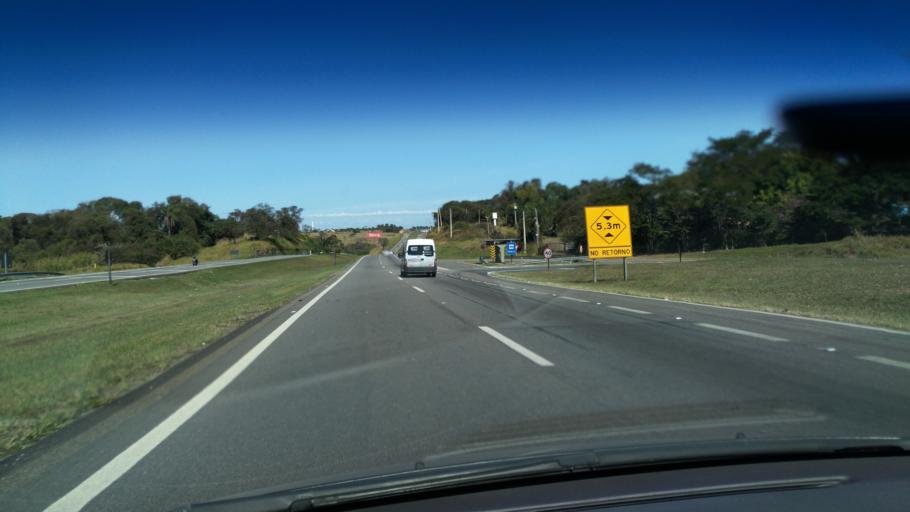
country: BR
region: Sao Paulo
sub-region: Jaguariuna
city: Jaguariuna
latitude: -22.6566
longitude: -47.0042
